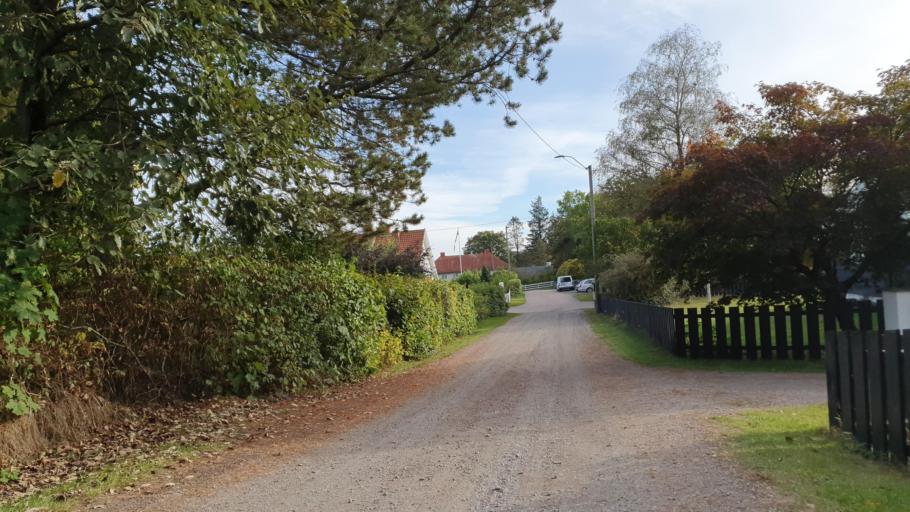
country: NO
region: Vestfold
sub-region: Tonsberg
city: Tonsberg
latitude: 59.2802
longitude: 10.4176
